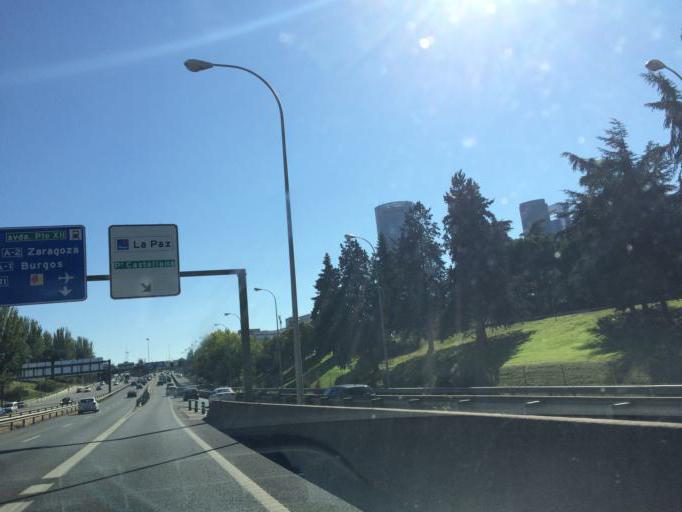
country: ES
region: Madrid
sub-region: Provincia de Madrid
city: Pinar de Chamartin
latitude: 40.4854
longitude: -3.6935
